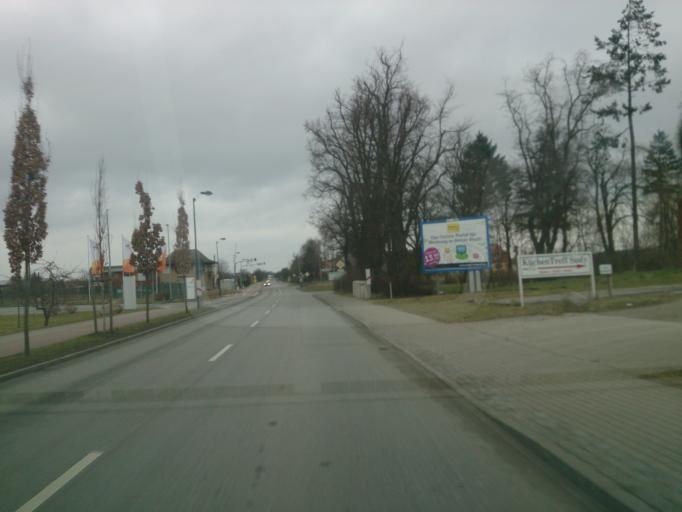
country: DE
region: Mecklenburg-Vorpommern
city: Wackerow
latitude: 53.7061
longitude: 12.9121
